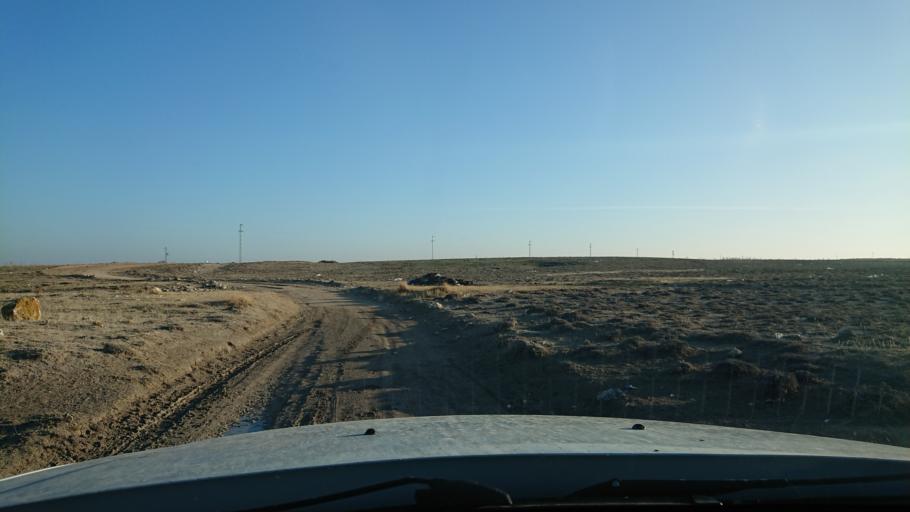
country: TR
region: Aksaray
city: Sultanhani
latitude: 38.2717
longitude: 33.5150
